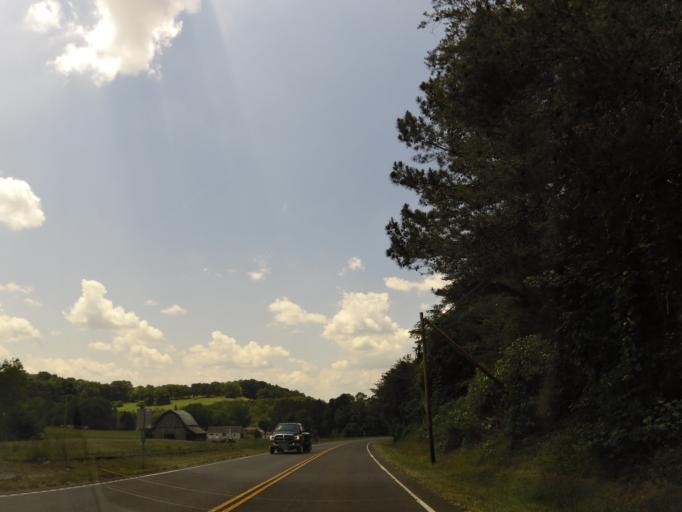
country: US
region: Tennessee
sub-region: Rhea County
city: Spring City
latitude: 35.6403
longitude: -84.8413
